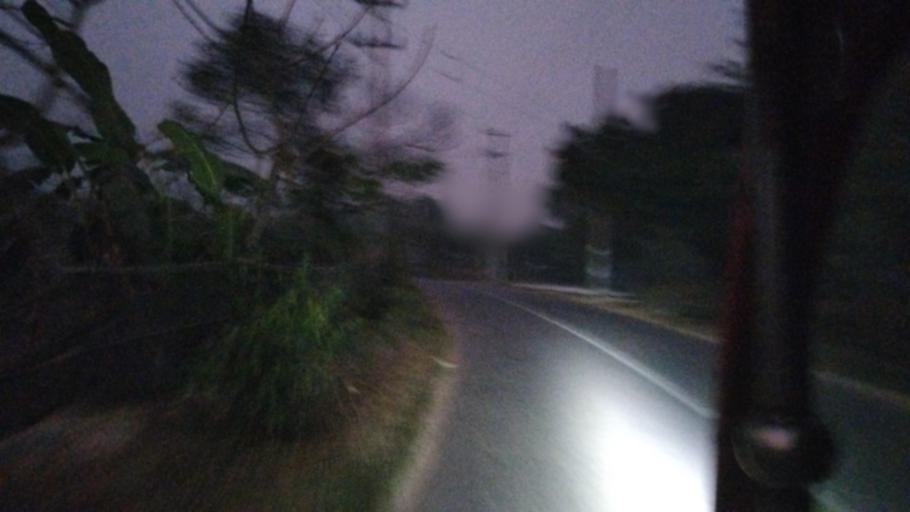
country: BD
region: Dhaka
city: Sakhipur
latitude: 24.3998
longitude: 90.3486
